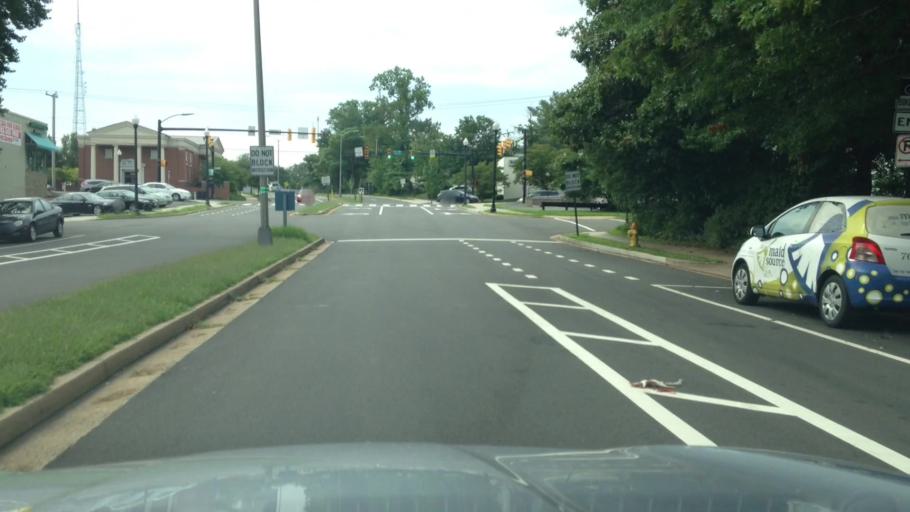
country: US
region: Virginia
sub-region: Fairfax County
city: Seven Corners
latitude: 38.8973
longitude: -77.1337
